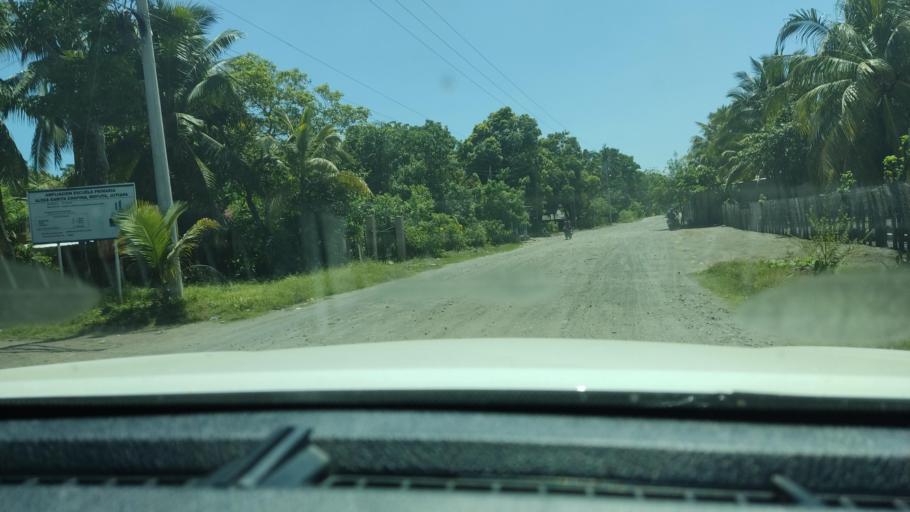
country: SV
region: Ahuachapan
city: San Francisco Menendez
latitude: 13.7511
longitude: -90.1219
